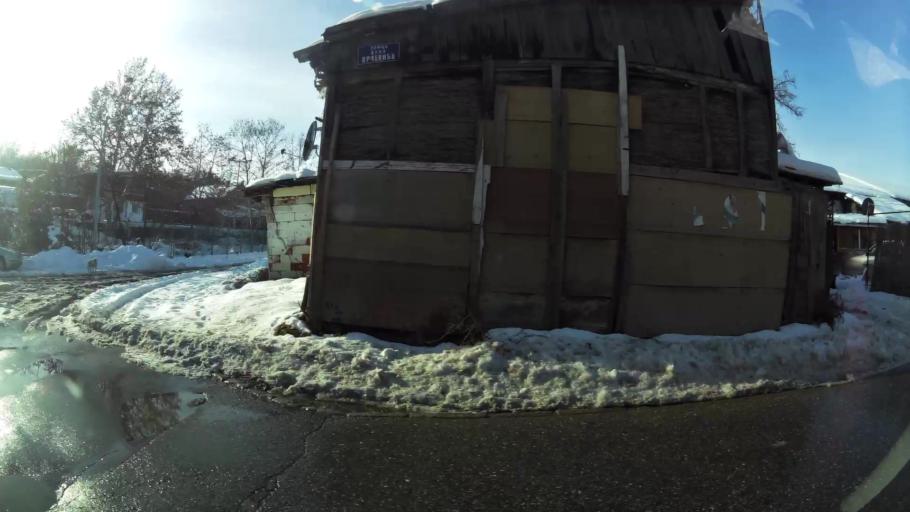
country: RS
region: Central Serbia
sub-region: Belgrade
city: Palilula
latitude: 44.8193
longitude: 20.4948
